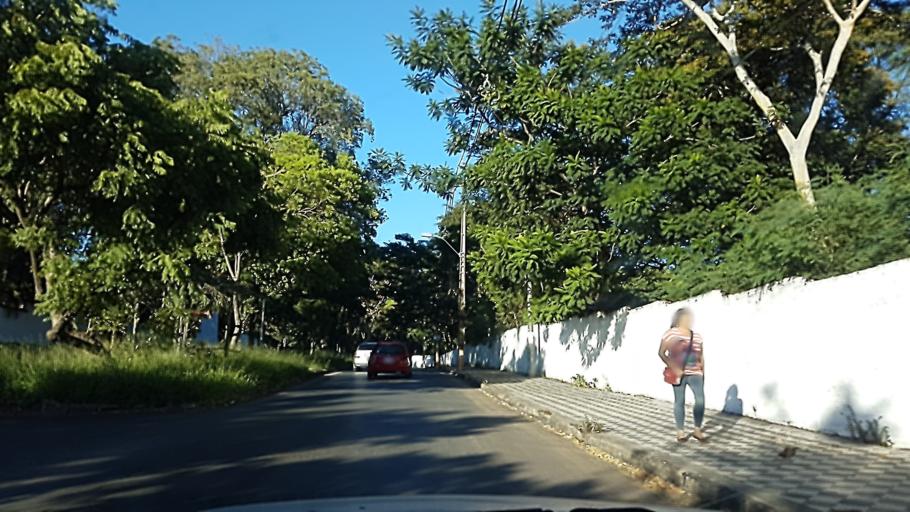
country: PY
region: Asuncion
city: Asuncion
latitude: -25.2729
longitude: -57.5759
